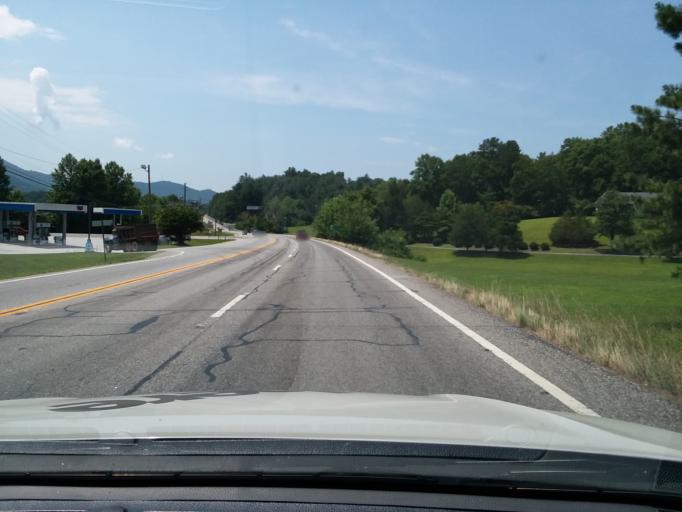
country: US
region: Georgia
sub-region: Rabun County
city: Mountain City
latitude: 34.9856
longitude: -83.3846
